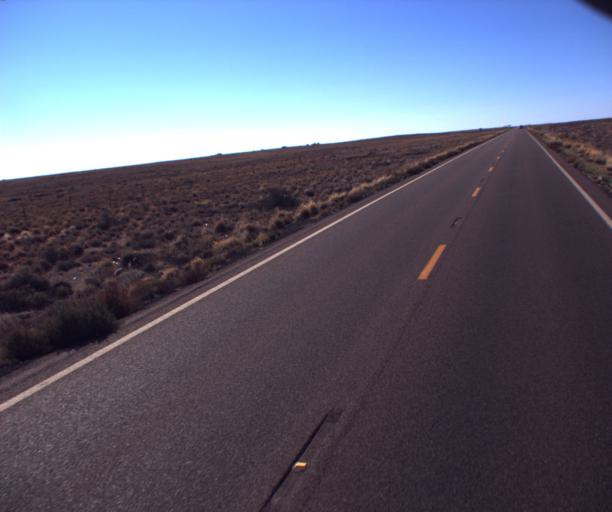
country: US
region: Arizona
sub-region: Navajo County
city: Dilkon
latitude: 35.2325
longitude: -110.4322
